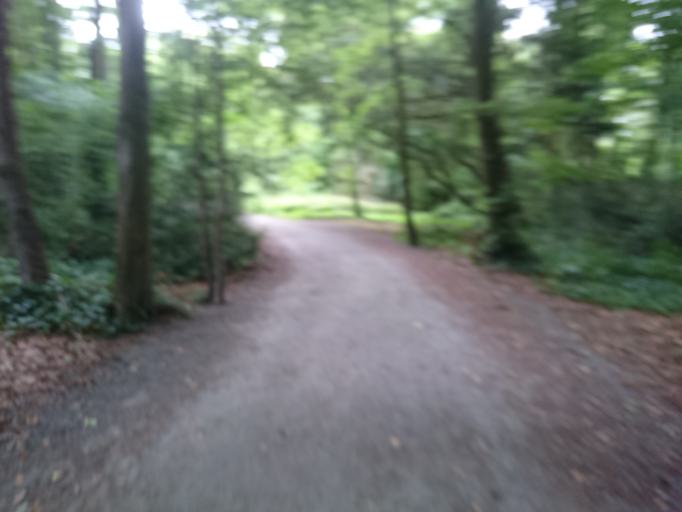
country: IE
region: Leinster
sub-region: Kilkenny
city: Kilkenny
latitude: 52.6500
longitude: -7.2396
